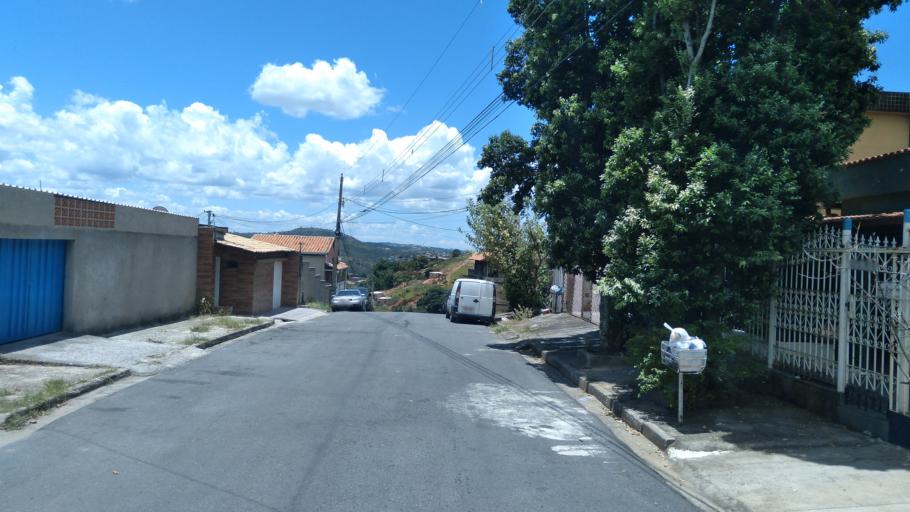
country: BR
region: Minas Gerais
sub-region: Santa Luzia
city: Santa Luzia
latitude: -19.8405
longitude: -43.8948
